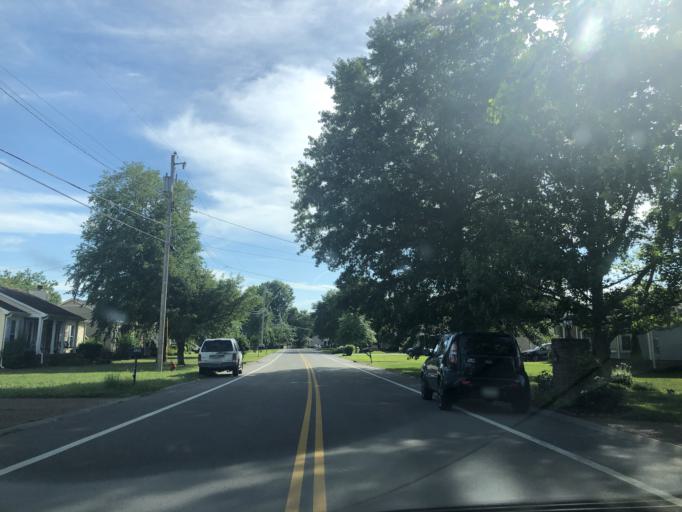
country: US
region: Tennessee
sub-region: Davidson County
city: Belle Meade
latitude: 36.0526
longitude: -86.9426
